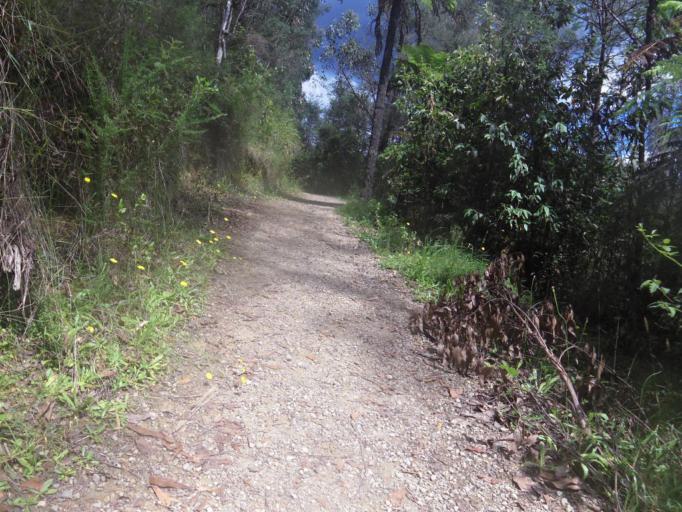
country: AU
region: Victoria
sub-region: Yarra Ranges
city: Millgrove
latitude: -37.5144
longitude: 145.7540
